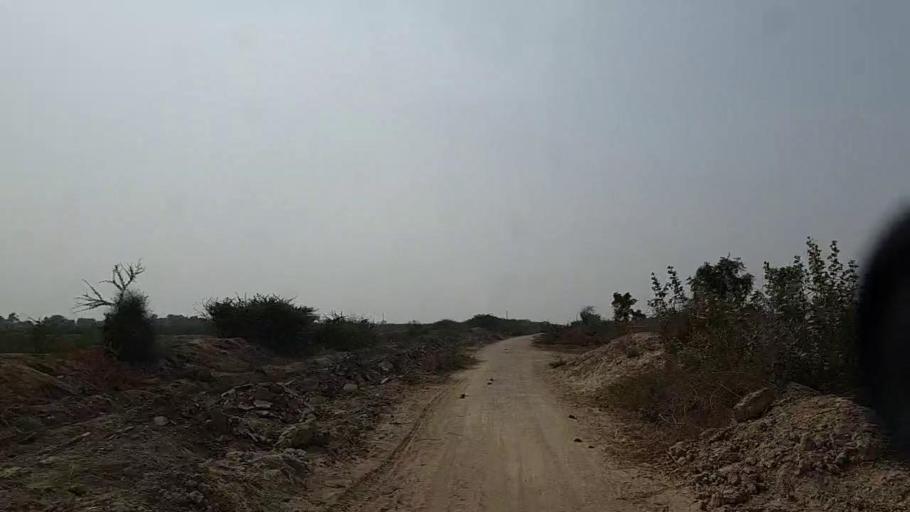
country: PK
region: Sindh
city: Naukot
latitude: 24.7724
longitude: 69.3071
